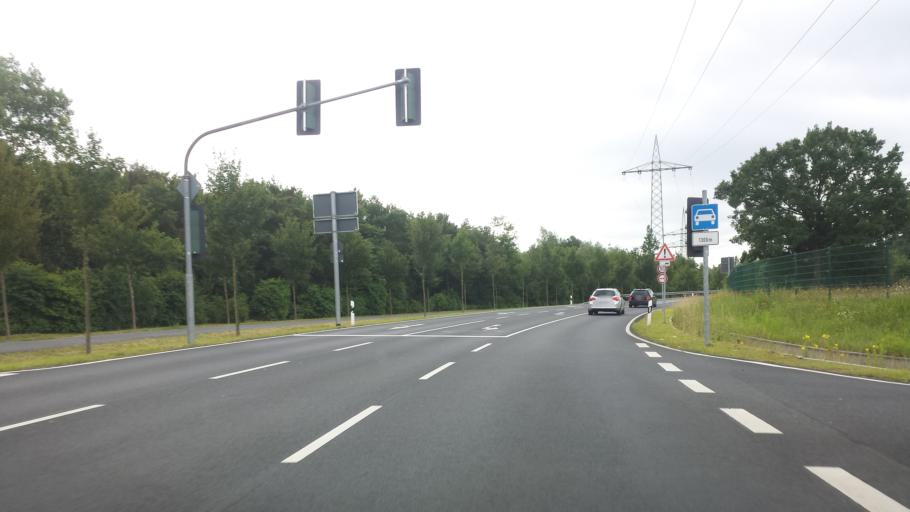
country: DE
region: Hesse
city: Kelsterbach
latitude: 50.0914
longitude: 8.5530
